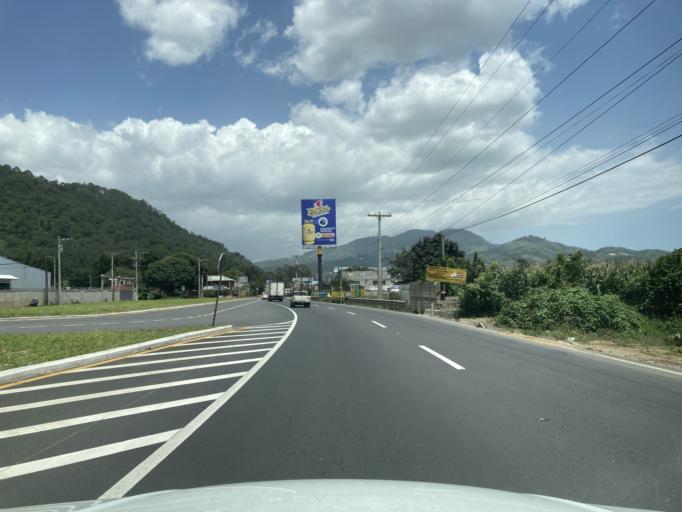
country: GT
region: Chimaltenango
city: El Tejar
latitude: 14.6384
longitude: -90.7652
